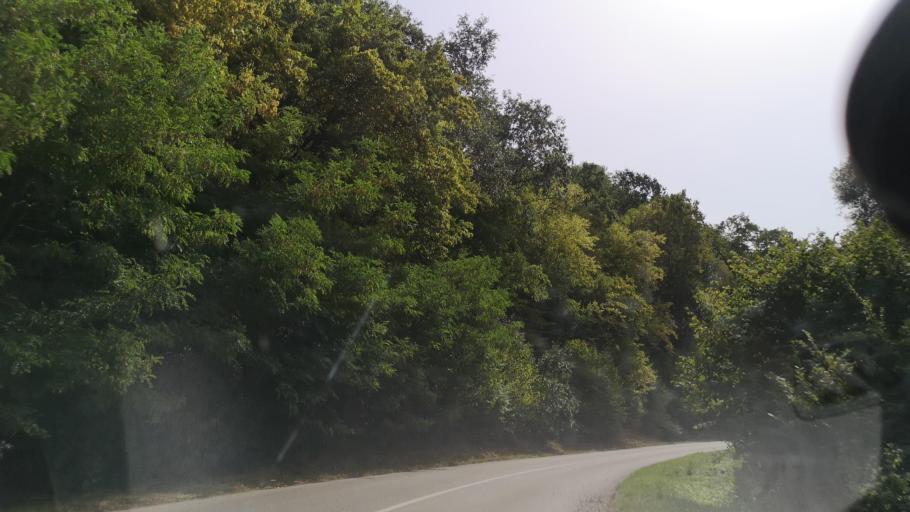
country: SK
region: Banskobystricky
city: Revuca
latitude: 48.6156
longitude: 20.2112
